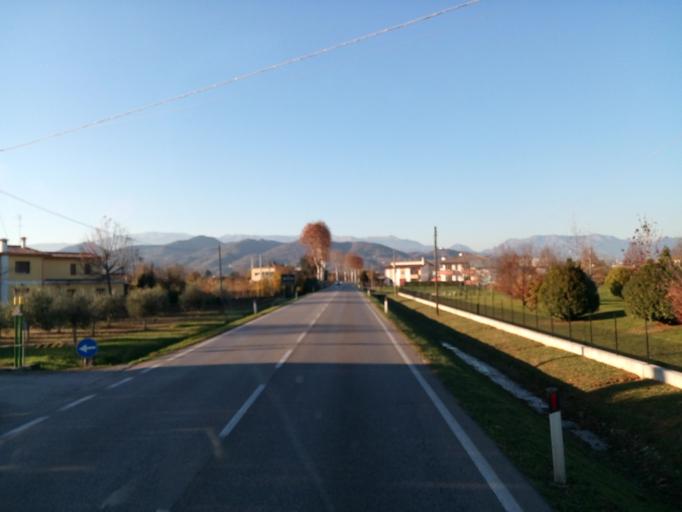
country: IT
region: Veneto
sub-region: Provincia di Treviso
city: Crocetta-Nogare
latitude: 45.8078
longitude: 12.0221
